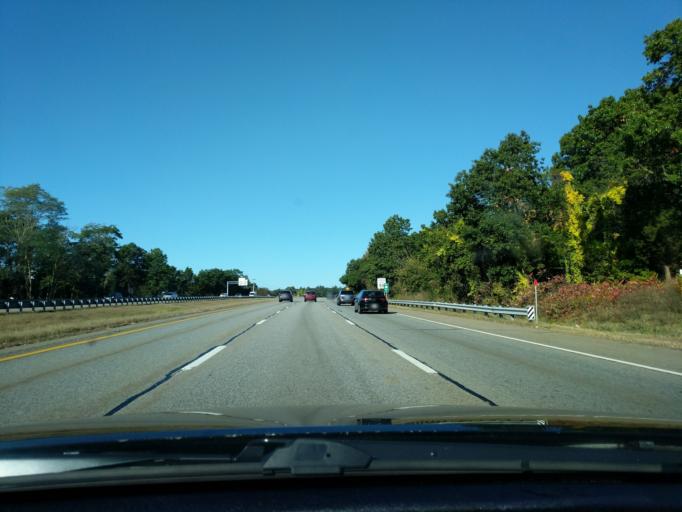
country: US
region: Massachusetts
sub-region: Middlesex County
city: Lexington
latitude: 42.4180
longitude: -71.2118
